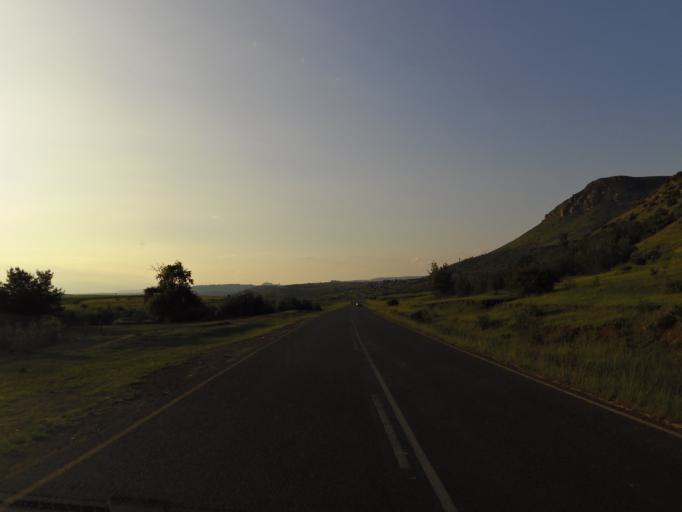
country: LS
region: Leribe
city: Leribe
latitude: -28.9801
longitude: 28.1795
